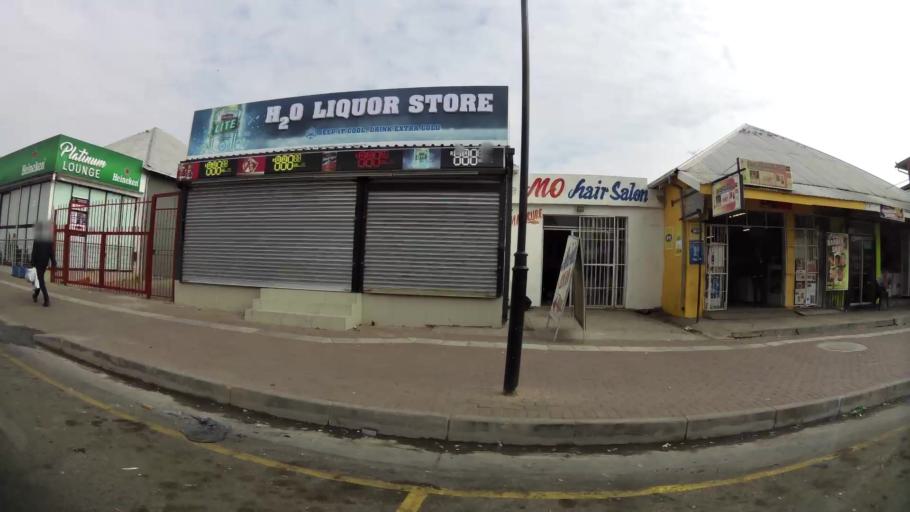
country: ZA
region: Orange Free State
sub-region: Mangaung Metropolitan Municipality
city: Bloemfontein
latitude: -29.1213
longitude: 26.2079
